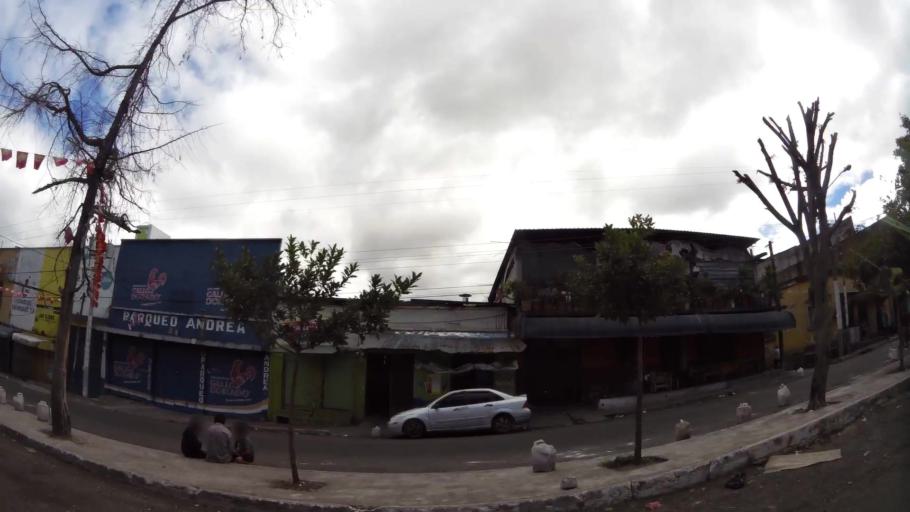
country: GT
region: Guatemala
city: Guatemala City
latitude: 14.6173
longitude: -90.5188
